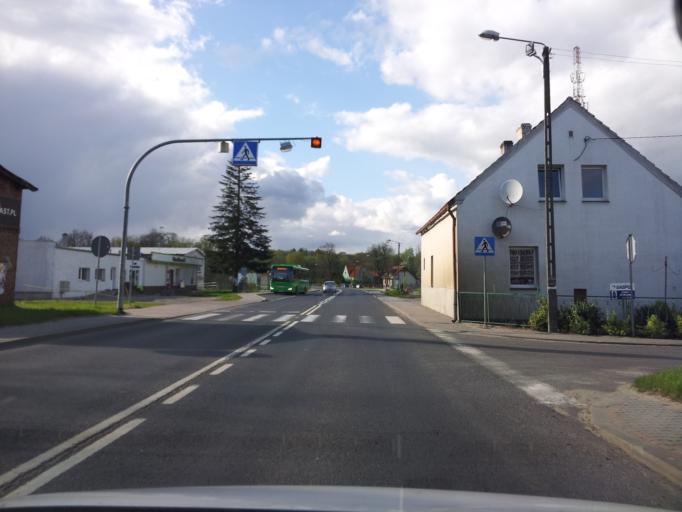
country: PL
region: Lubusz
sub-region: Powiat krosnienski
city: Dabie
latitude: 52.0104
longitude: 15.1523
